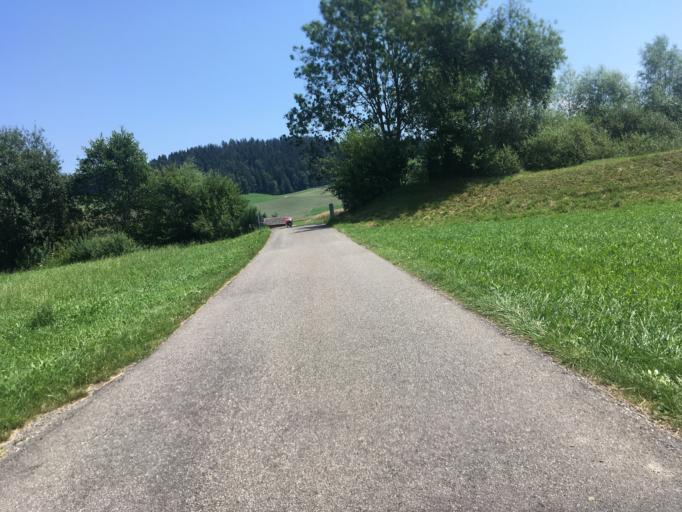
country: CH
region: Bern
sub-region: Bern-Mittelland District
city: Bowil
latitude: 46.8998
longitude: 7.7011
